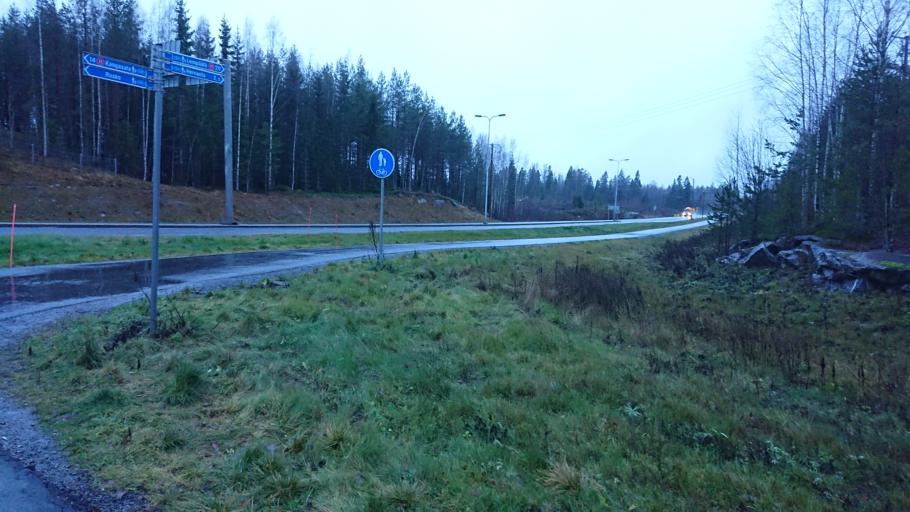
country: FI
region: Pirkanmaa
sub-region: Tampere
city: Tampere
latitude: 61.4427
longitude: 23.8754
